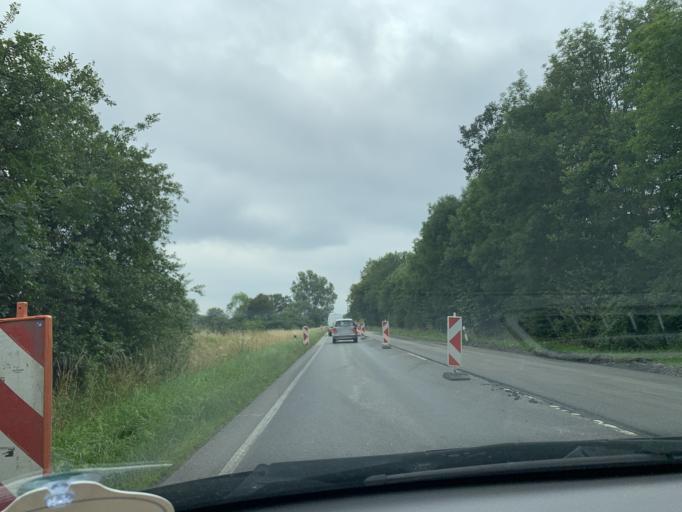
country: DE
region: North Rhine-Westphalia
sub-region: Regierungsbezirk Munster
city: Ennigerloh
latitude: 51.8976
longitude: 8.0531
